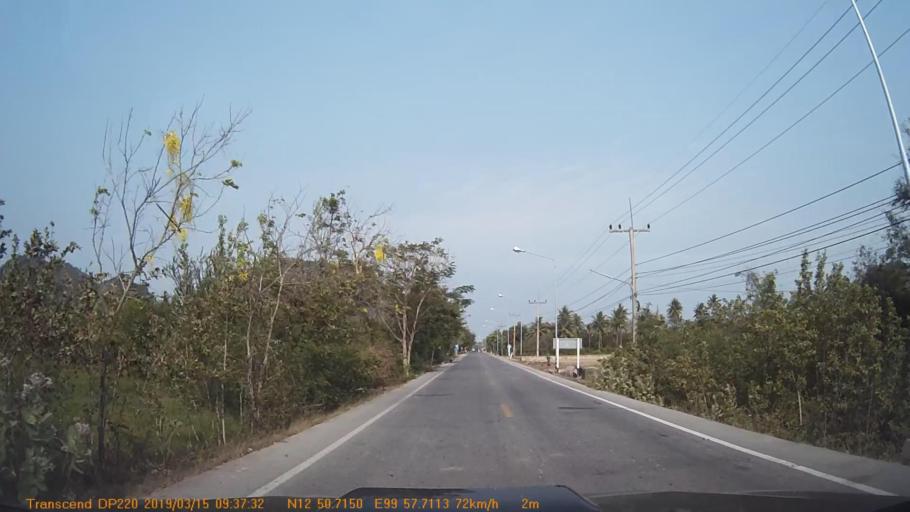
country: TH
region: Phetchaburi
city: Cha-am
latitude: 12.8454
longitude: 99.9616
